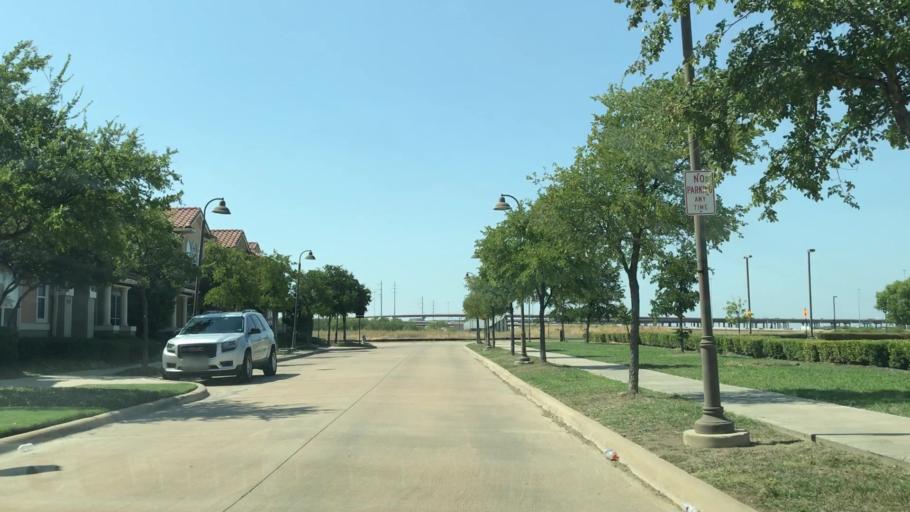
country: US
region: Texas
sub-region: Dallas County
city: Farmers Branch
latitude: 32.9028
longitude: -96.9381
